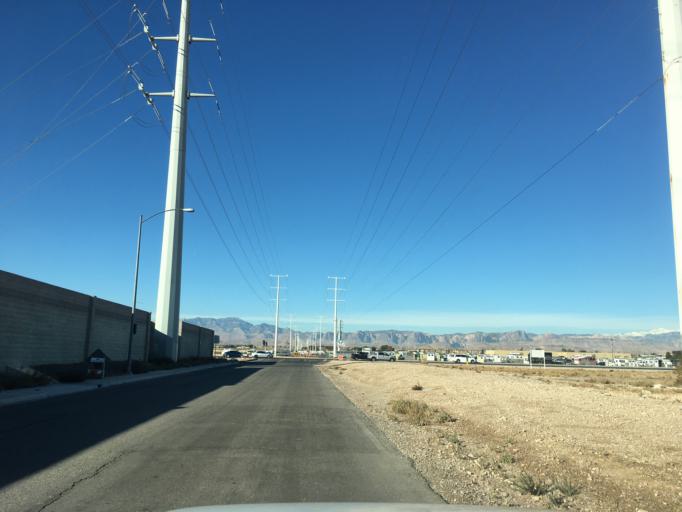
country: US
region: Nevada
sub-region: Clark County
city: Enterprise
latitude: 36.0029
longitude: -115.1710
